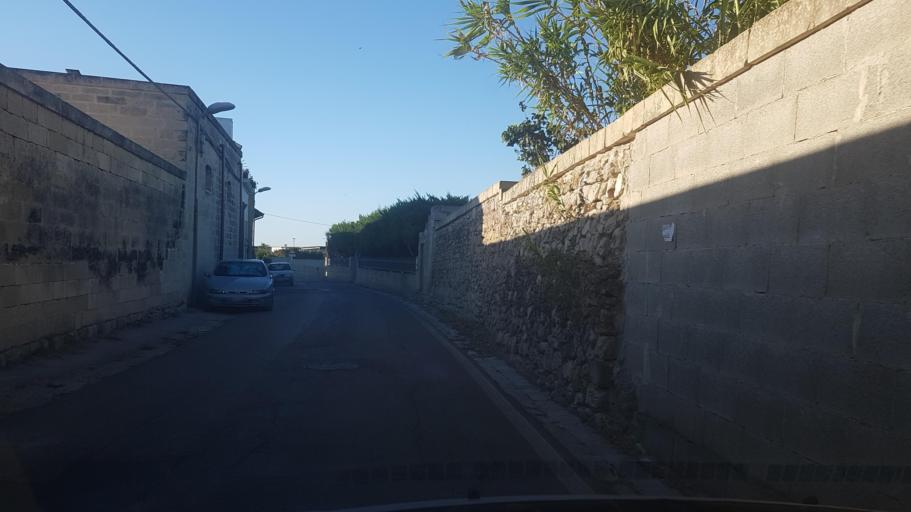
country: IT
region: Apulia
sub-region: Provincia di Lecce
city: Struda
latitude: 40.3229
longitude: 18.3198
